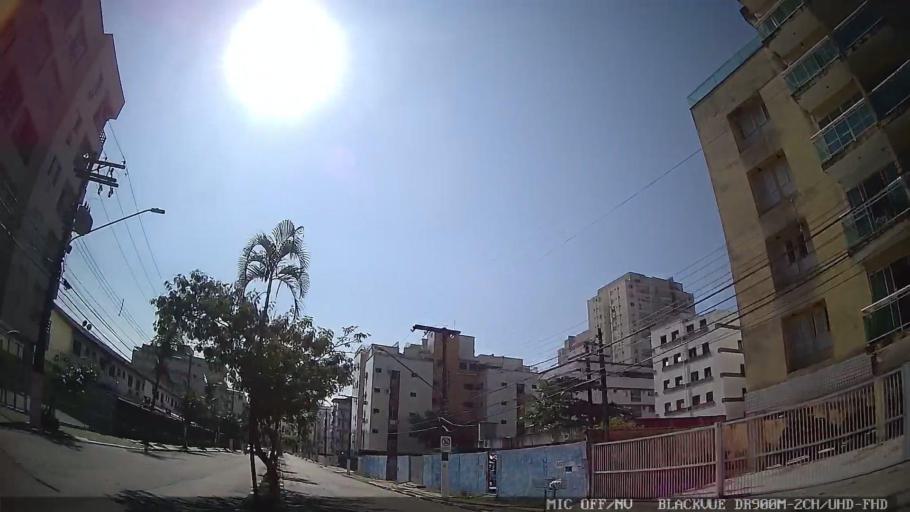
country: BR
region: Sao Paulo
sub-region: Guaruja
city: Guaruja
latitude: -24.0102
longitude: -46.2764
